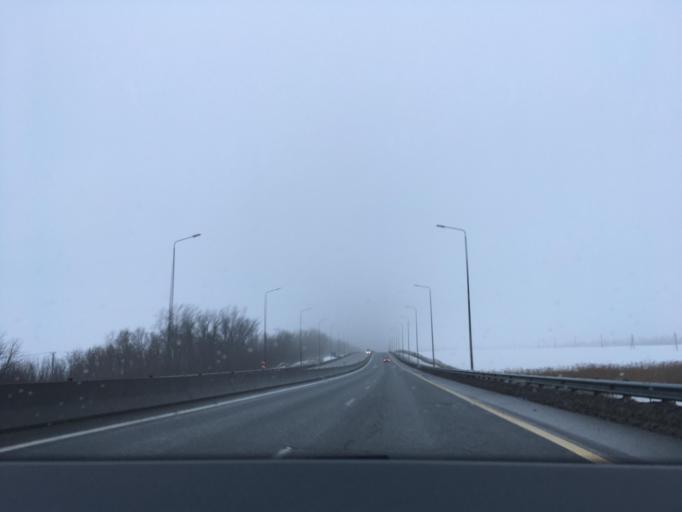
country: RU
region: Krasnodarskiy
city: Krasnoye
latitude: 46.7985
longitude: 39.6678
